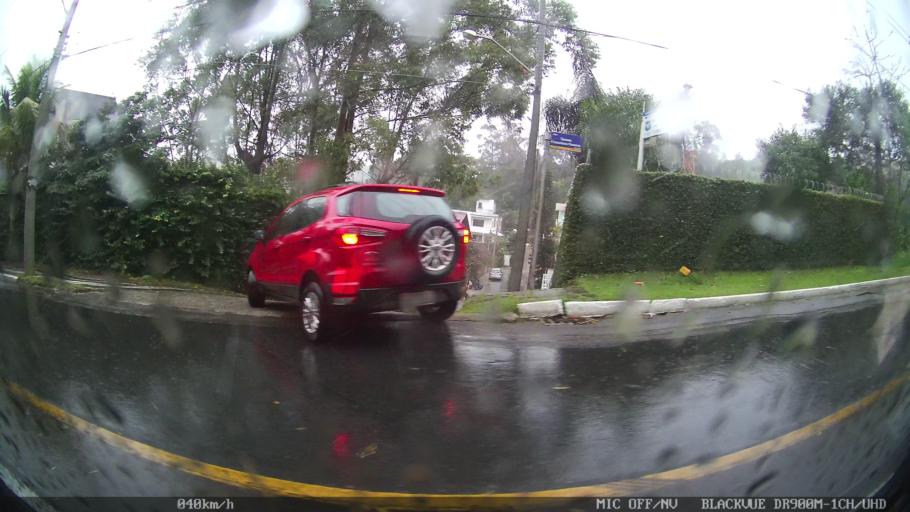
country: BR
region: Santa Catarina
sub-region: Itajai
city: Itajai
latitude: -26.9301
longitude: -48.6372
